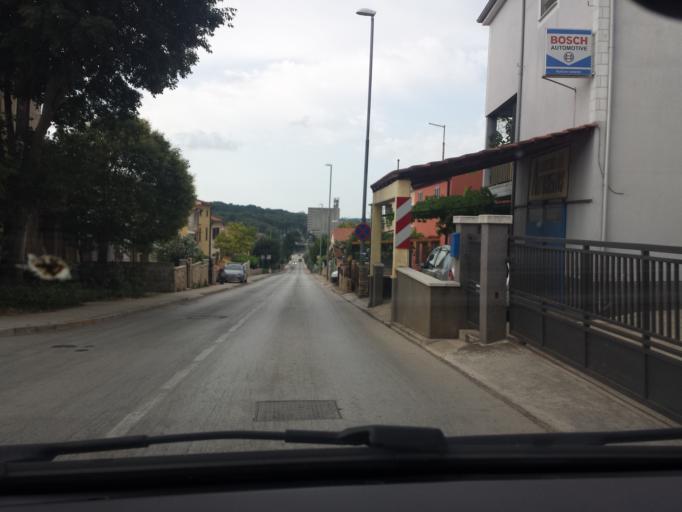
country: HR
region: Istarska
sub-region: Grad Pula
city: Pula
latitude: 44.8909
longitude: 13.8502
